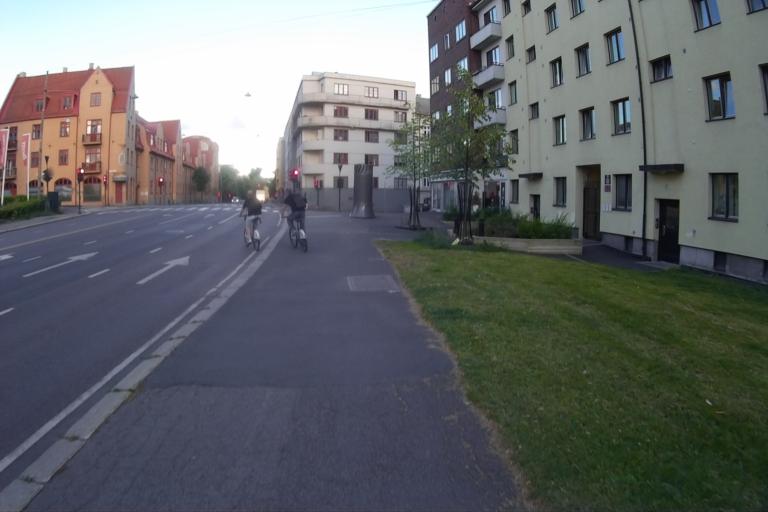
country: NO
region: Oslo
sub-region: Oslo
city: Oslo
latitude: 59.9327
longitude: 10.7589
